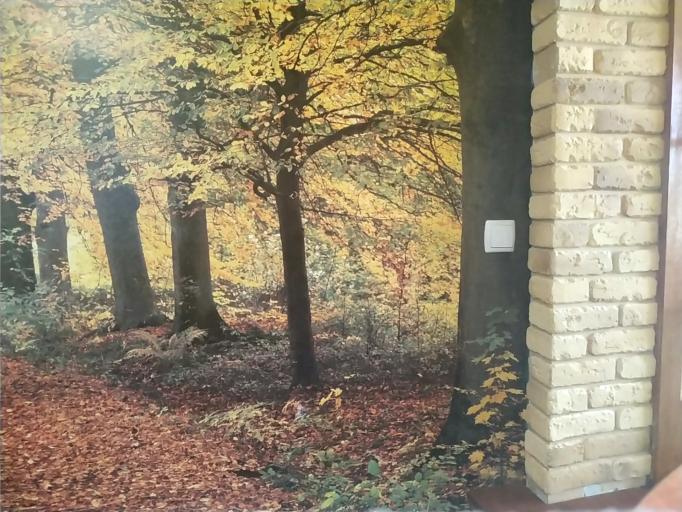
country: RU
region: Tverskaya
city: Vyshniy Volochek
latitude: 57.6563
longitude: 34.5452
